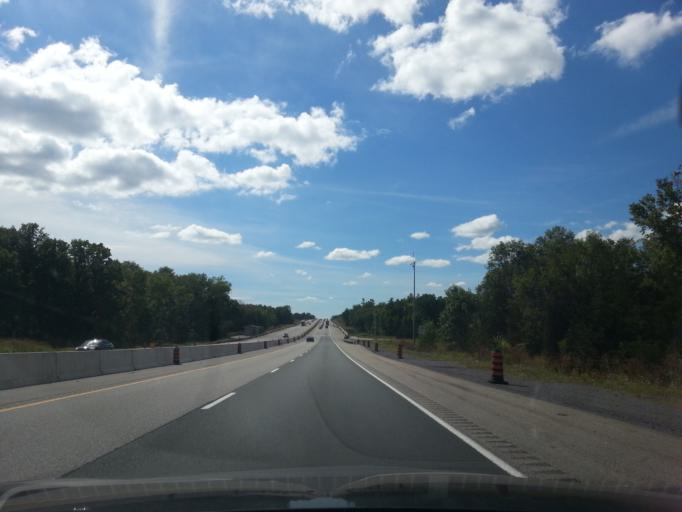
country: CA
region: Ontario
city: Deseronto
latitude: 44.2291
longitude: -77.1757
